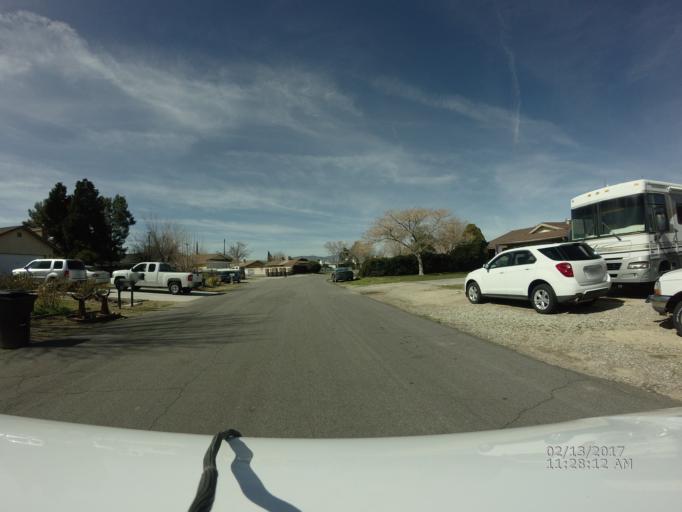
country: US
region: California
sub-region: Los Angeles County
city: Littlerock
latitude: 34.5260
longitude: -117.9995
